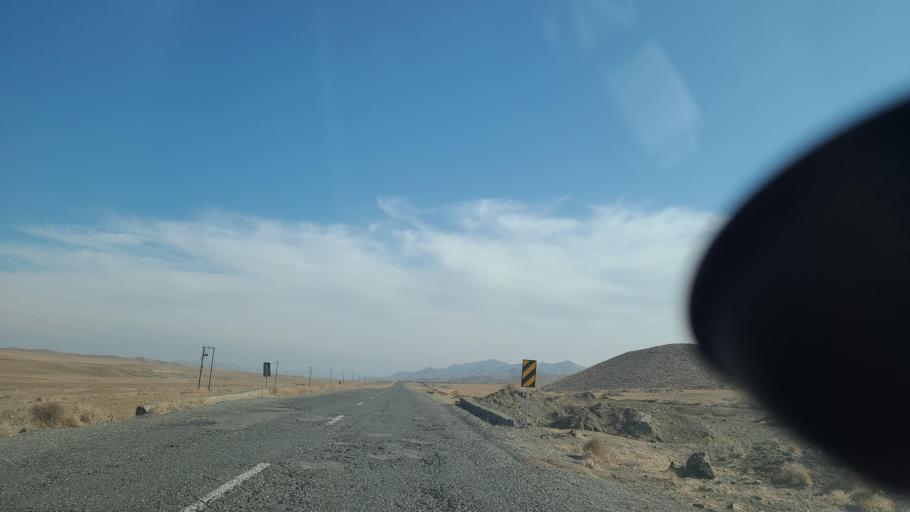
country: IR
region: Razavi Khorasan
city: Fariman
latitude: 35.5901
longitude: 59.6150
